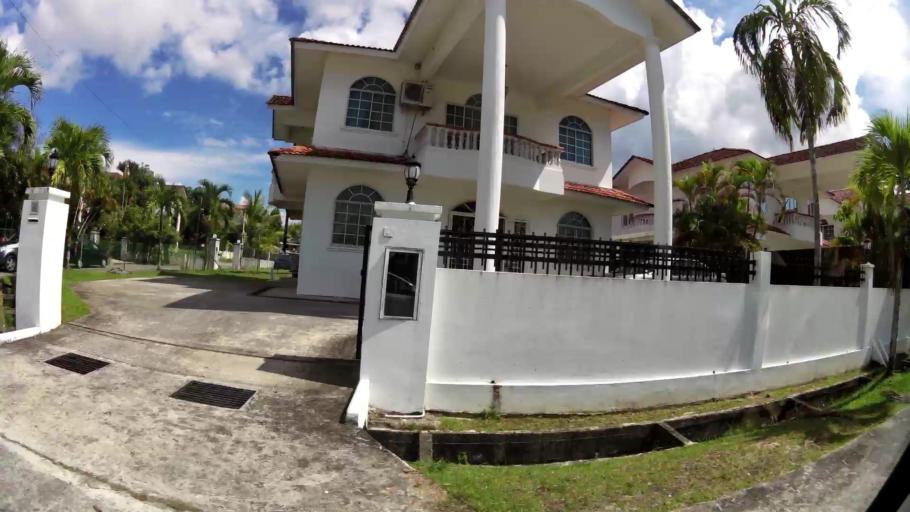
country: BN
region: Brunei and Muara
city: Bandar Seri Begawan
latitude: 4.9683
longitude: 114.9447
